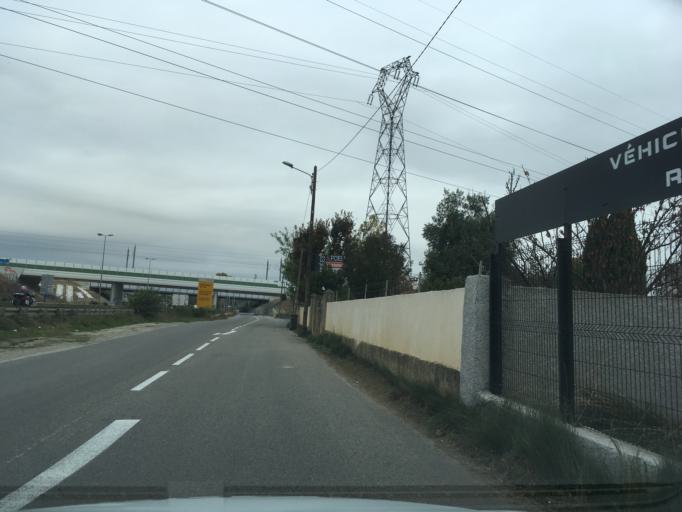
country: FR
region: Languedoc-Roussillon
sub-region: Departement de l'Herault
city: Lattes
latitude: 43.5818
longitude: 3.8984
